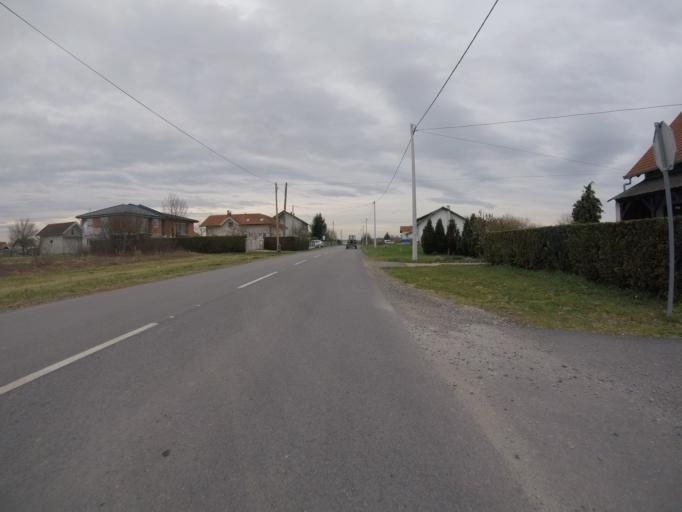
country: HR
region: Zagrebacka
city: Lukavec
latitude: 45.7097
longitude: 16.0139
